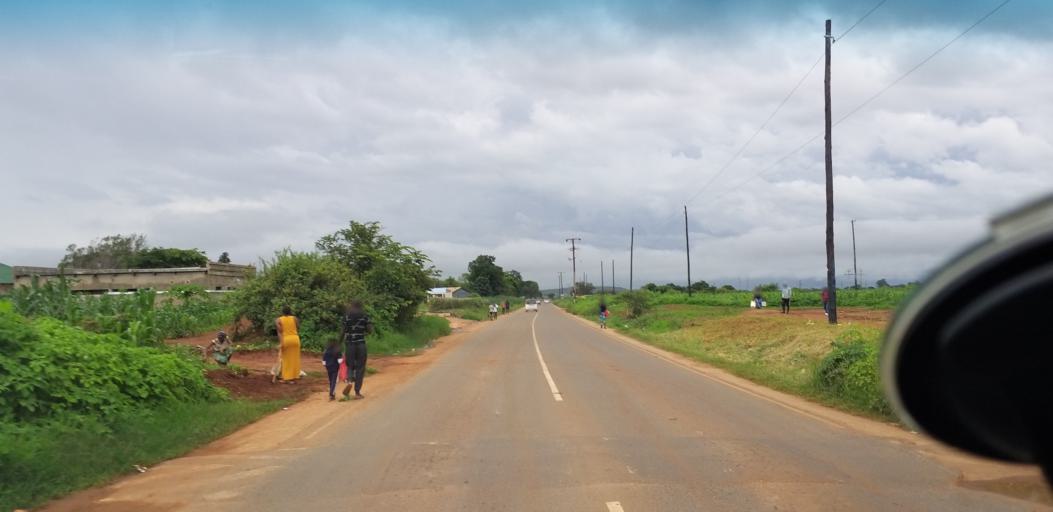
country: ZM
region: Lusaka
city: Lusaka
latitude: -15.5164
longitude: 28.2978
